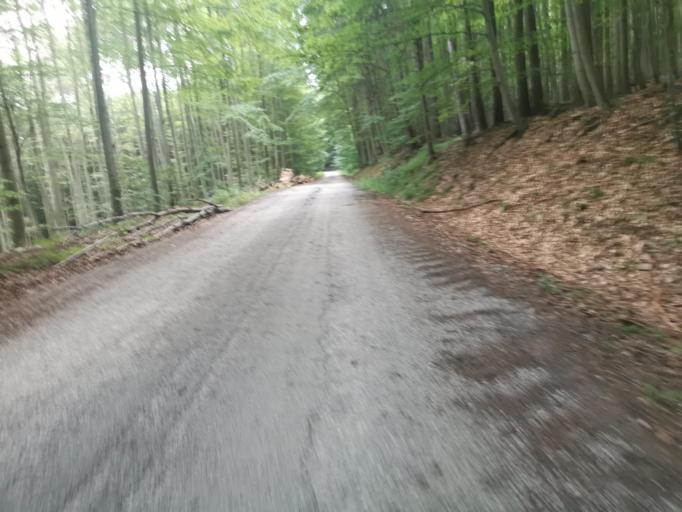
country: SK
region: Trenciansky
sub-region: Okres Myjava
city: Myjava
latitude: 48.7924
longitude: 17.6076
